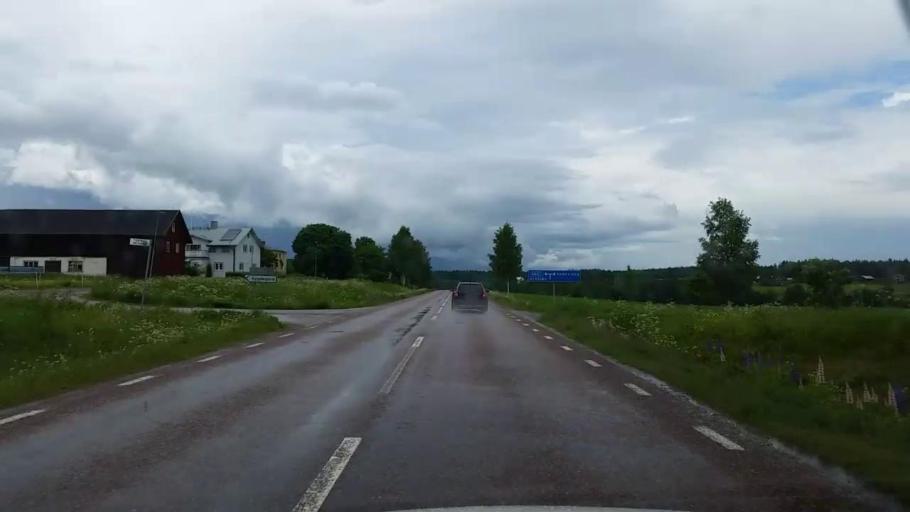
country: SE
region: Gaevleborg
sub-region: Sandvikens Kommun
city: Jarbo
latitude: 60.6930
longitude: 16.6138
